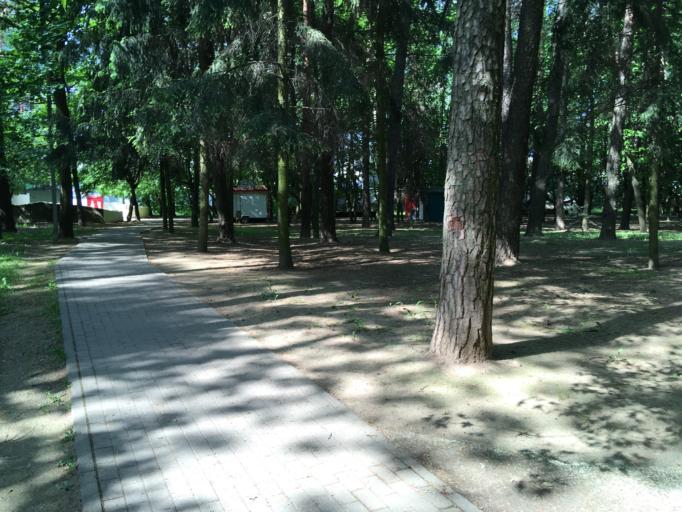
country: BY
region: Minsk
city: Minsk
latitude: 53.9215
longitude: 27.6103
